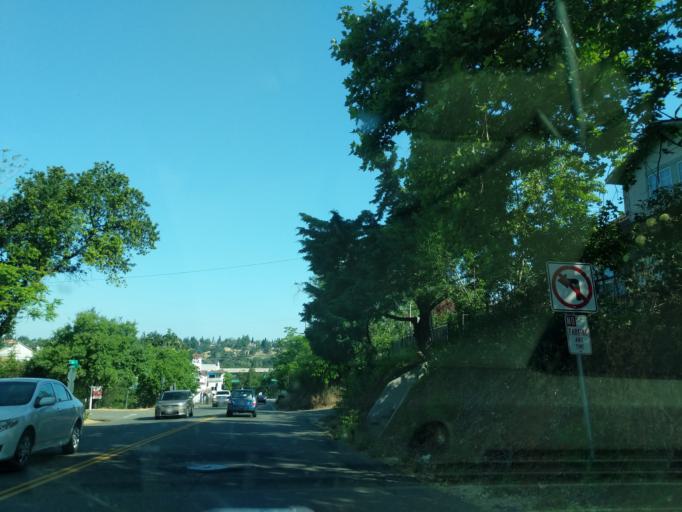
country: US
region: California
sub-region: Sacramento County
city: Folsom
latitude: 38.6767
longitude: -121.1754
